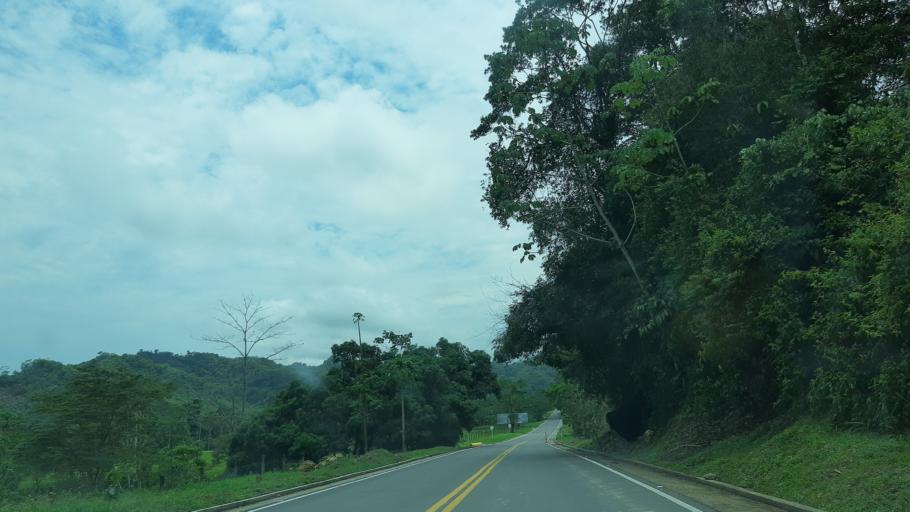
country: CO
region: Boyaca
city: San Luis de Gaceno
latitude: 4.8311
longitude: -73.1417
